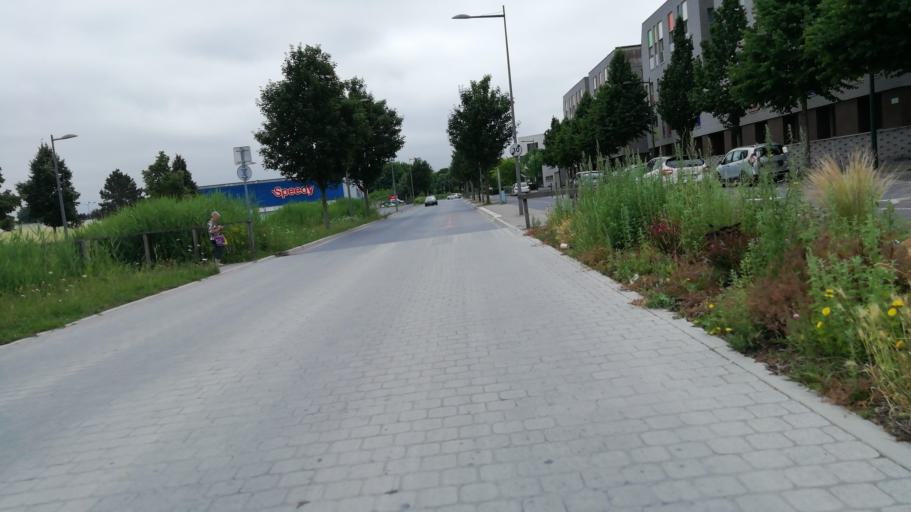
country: FR
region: Champagne-Ardenne
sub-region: Departement de la Marne
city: Betheny
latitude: 49.2600
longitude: 4.0626
